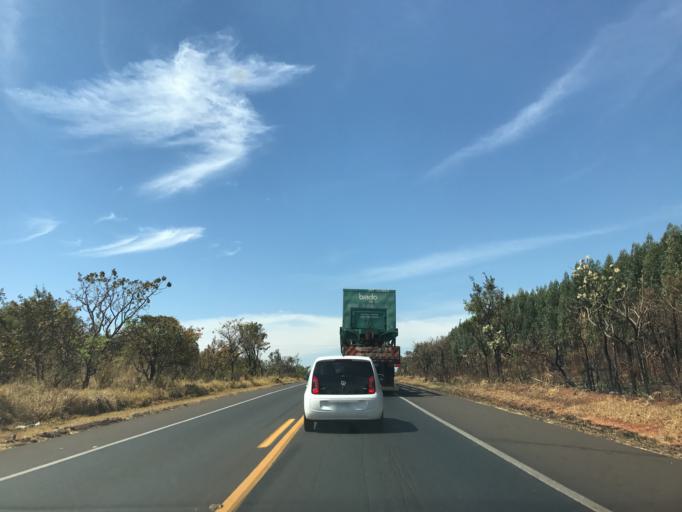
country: BR
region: Minas Gerais
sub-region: Prata
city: Prata
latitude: -19.1066
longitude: -48.9768
